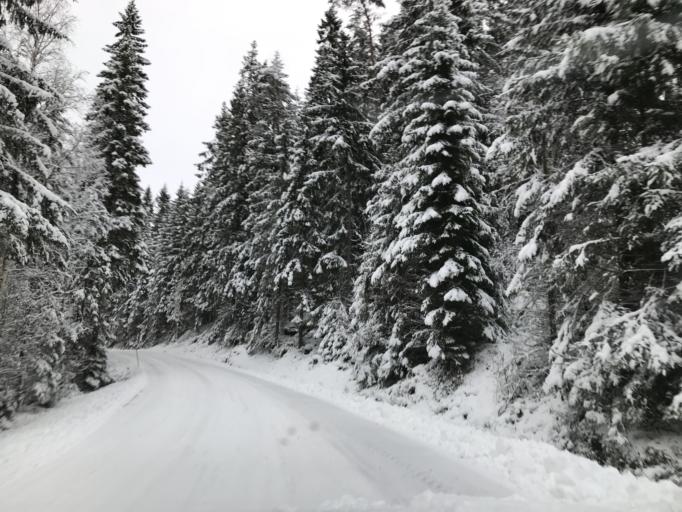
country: SE
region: Vaestra Goetaland
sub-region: Boras Kommun
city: Sandared
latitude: 57.8061
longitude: 12.7221
